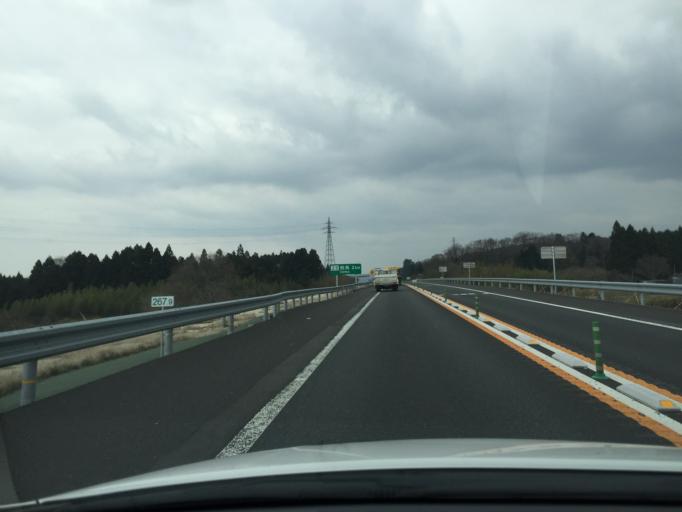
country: JP
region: Miyagi
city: Marumori
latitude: 37.8013
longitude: 140.8856
